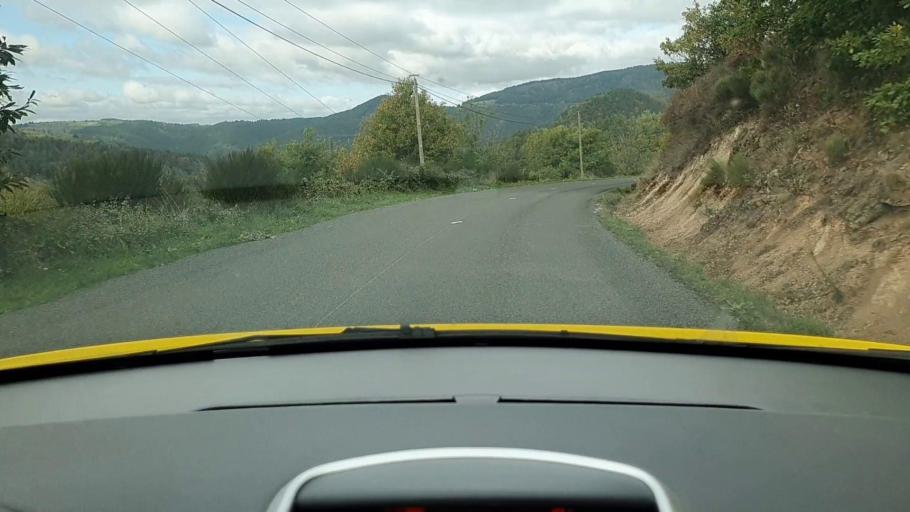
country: FR
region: Languedoc-Roussillon
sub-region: Departement de la Lozere
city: Meyrueis
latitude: 44.1064
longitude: 3.4380
